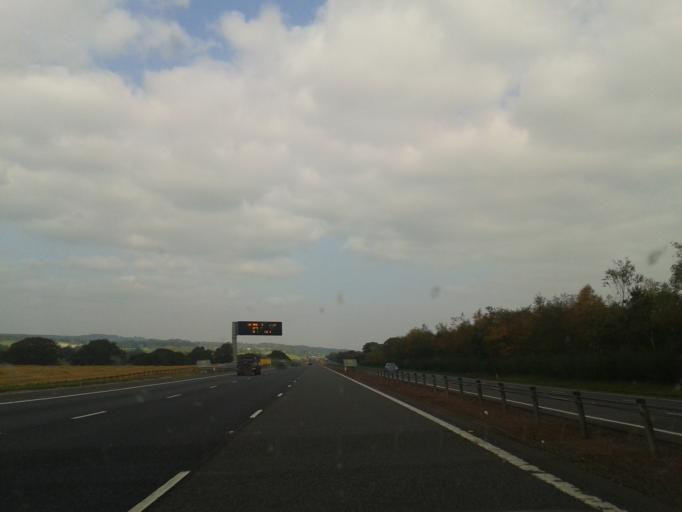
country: GB
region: Scotland
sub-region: Dumfries and Galloway
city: Lochmaben
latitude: 55.1839
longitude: -3.4063
